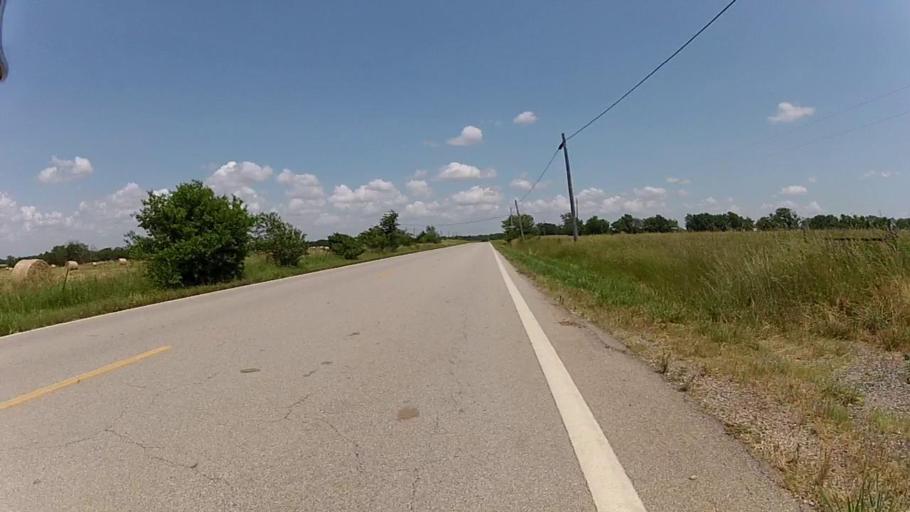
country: US
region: Kansas
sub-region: Labette County
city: Altamont
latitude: 37.1924
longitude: -95.4228
